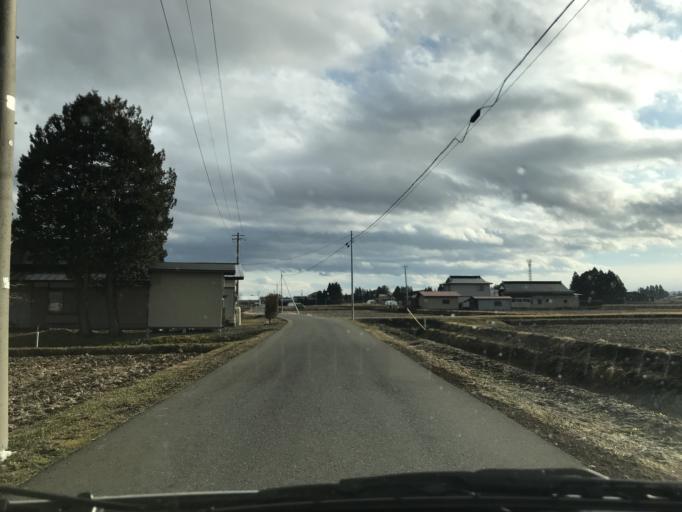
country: JP
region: Iwate
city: Mizusawa
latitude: 39.1447
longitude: 141.0821
